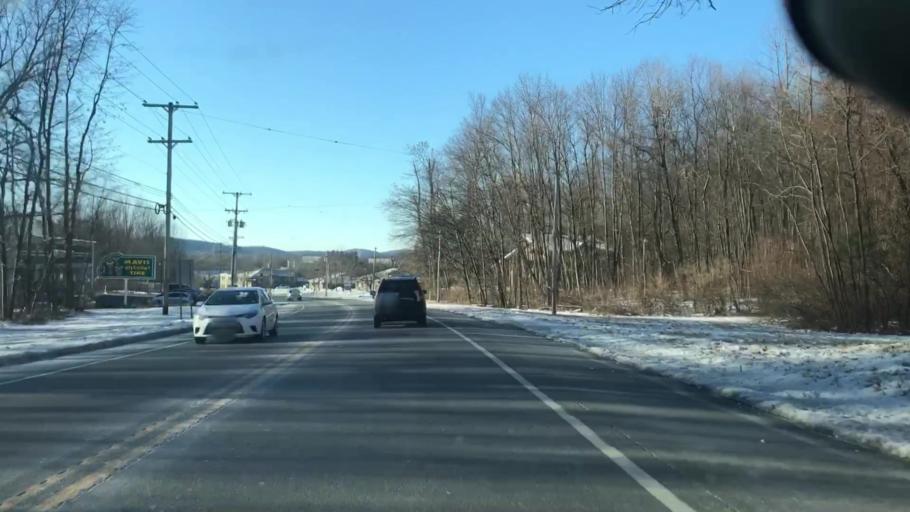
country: US
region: New Jersey
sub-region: Morris County
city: Budd Lake
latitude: 40.8378
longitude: -74.7090
